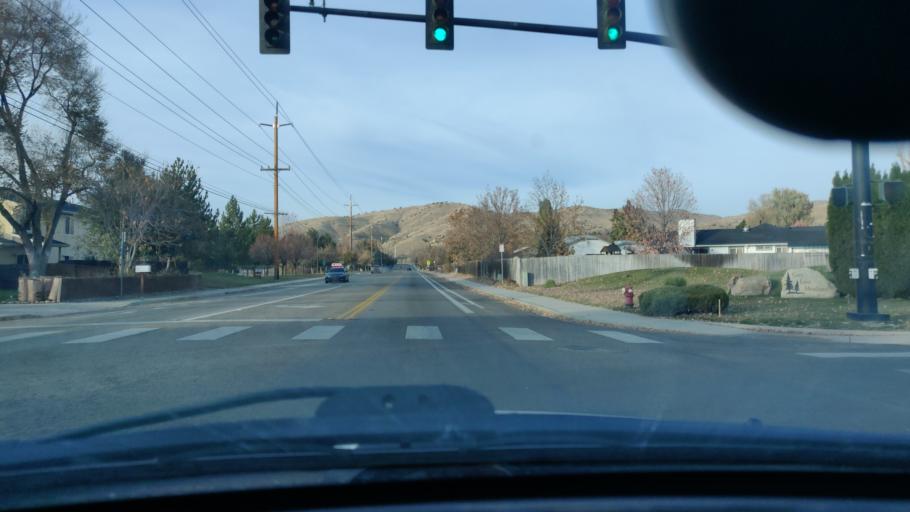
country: US
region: Idaho
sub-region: Ada County
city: Garden City
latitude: 43.6779
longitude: -116.2792
